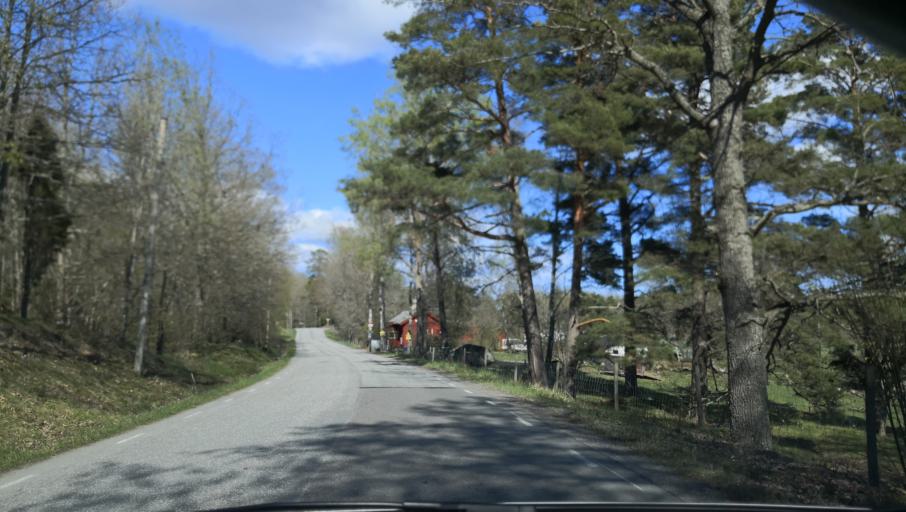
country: SE
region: Stockholm
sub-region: Varmdo Kommun
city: Hemmesta
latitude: 59.3912
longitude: 18.5109
